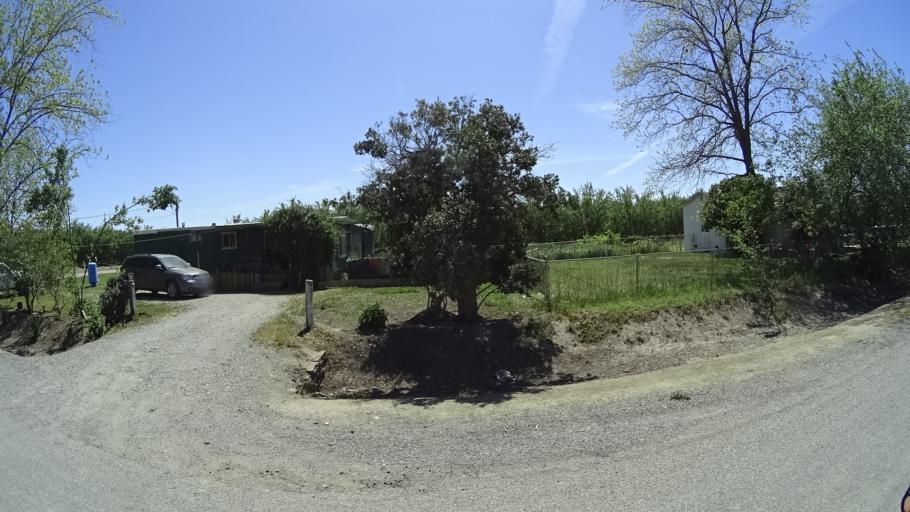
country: US
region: California
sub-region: Glenn County
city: Hamilton City
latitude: 39.7214
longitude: -122.0929
